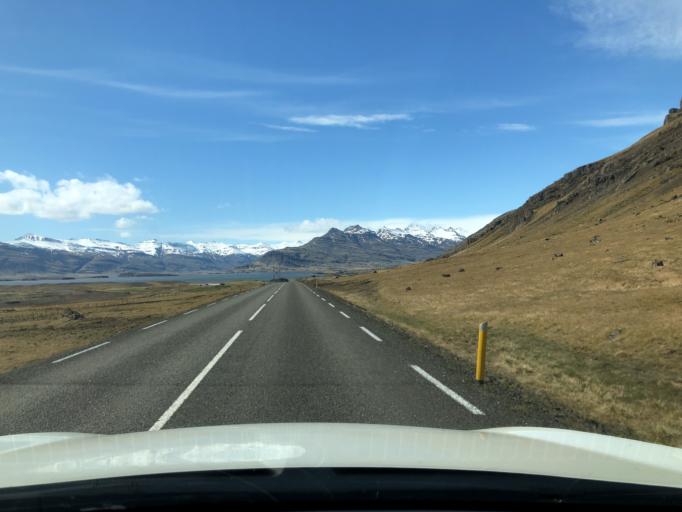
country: IS
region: East
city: Reydarfjoerdur
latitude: 64.5978
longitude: -14.4644
